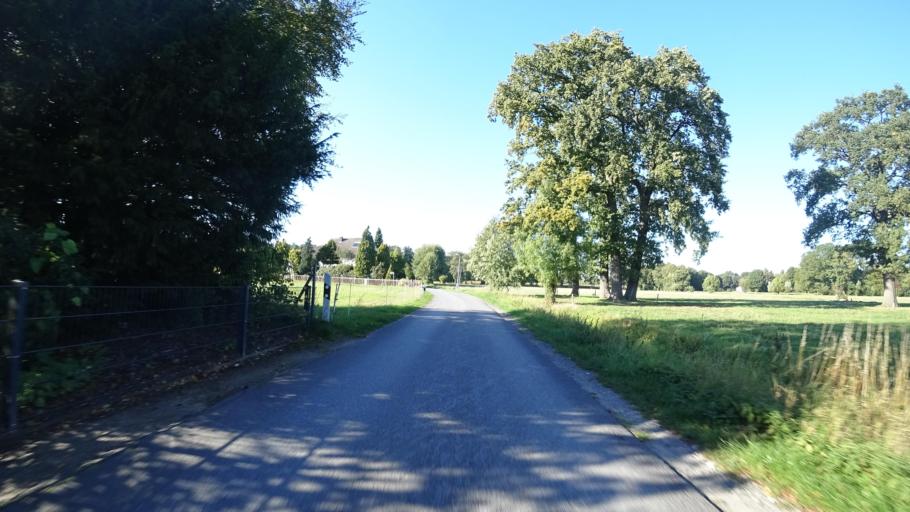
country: DE
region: North Rhine-Westphalia
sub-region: Regierungsbezirk Detmold
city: Guetersloh
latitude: 51.8747
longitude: 8.3620
